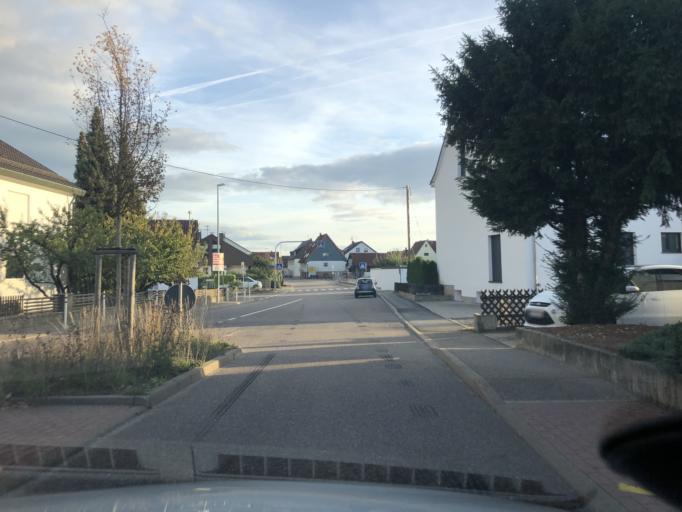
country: DE
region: Baden-Wuerttemberg
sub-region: Karlsruhe Region
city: Friolzheim
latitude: 48.8378
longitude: 8.8315
